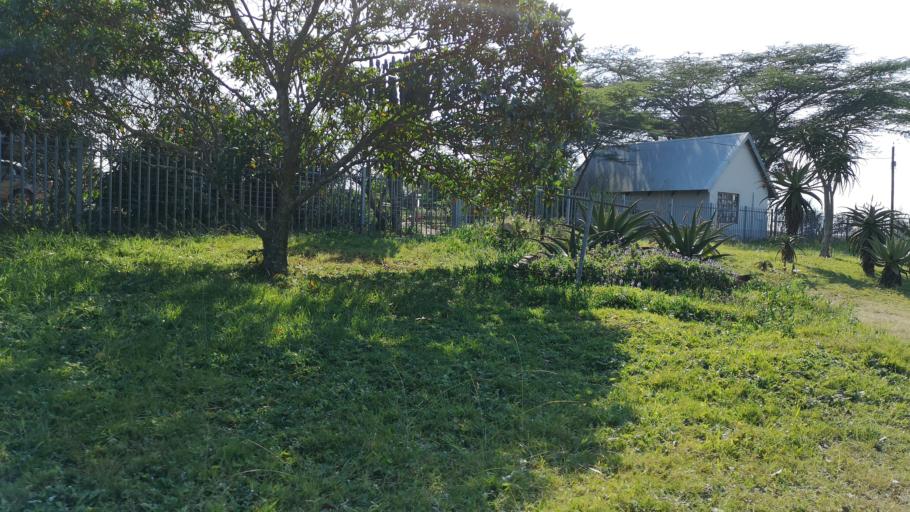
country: ZA
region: KwaZulu-Natal
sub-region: eThekwini Metropolitan Municipality
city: Mpumalanga
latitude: -29.7362
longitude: 30.6852
